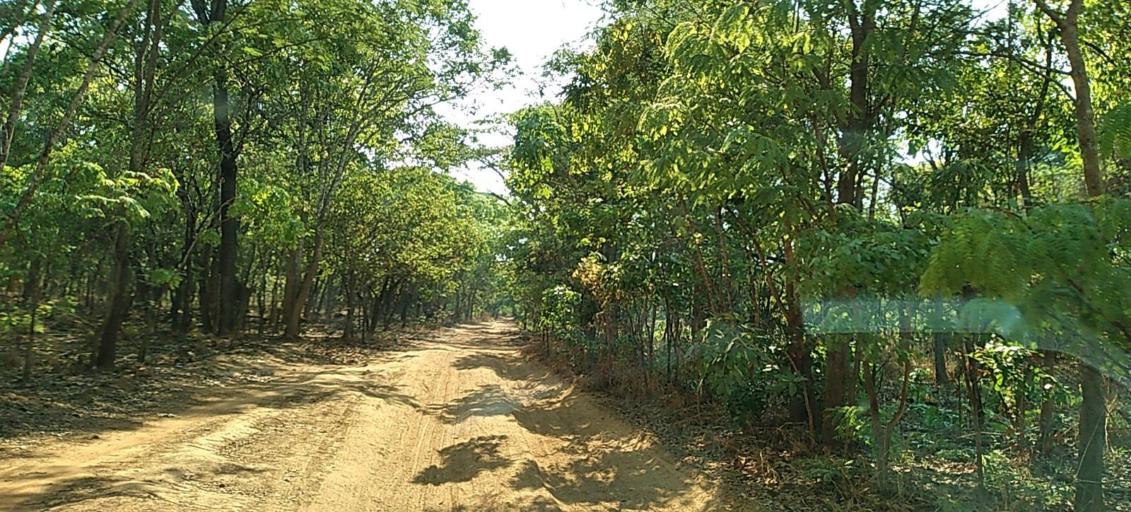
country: ZM
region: Copperbelt
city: Kalulushi
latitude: -13.0049
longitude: 27.7573
